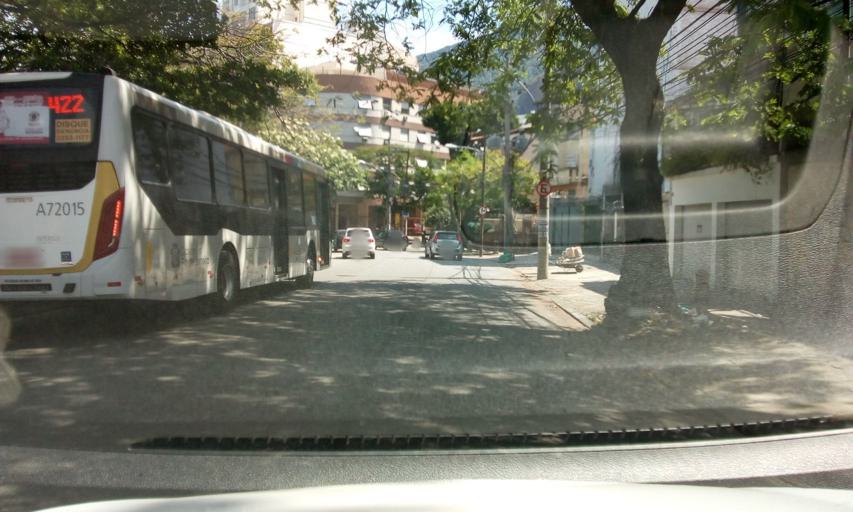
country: BR
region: Rio de Janeiro
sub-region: Rio De Janeiro
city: Rio de Janeiro
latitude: -22.9173
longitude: -43.2630
